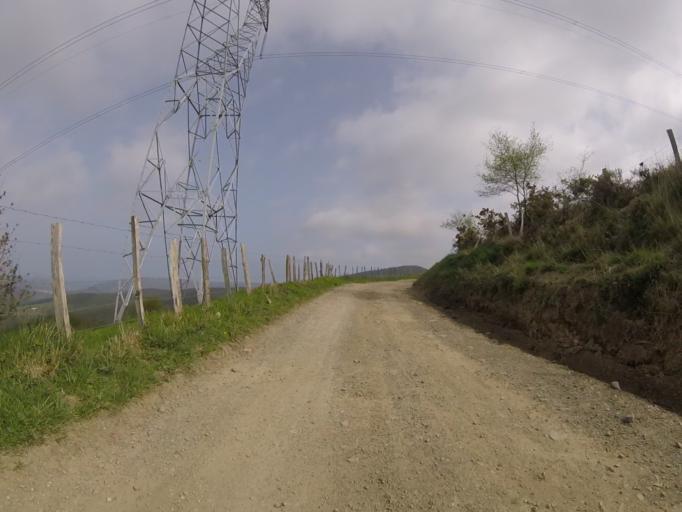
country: ES
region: Basque Country
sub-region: Provincia de Guipuzcoa
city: Zizurkil
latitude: 43.2324
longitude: -2.0882
